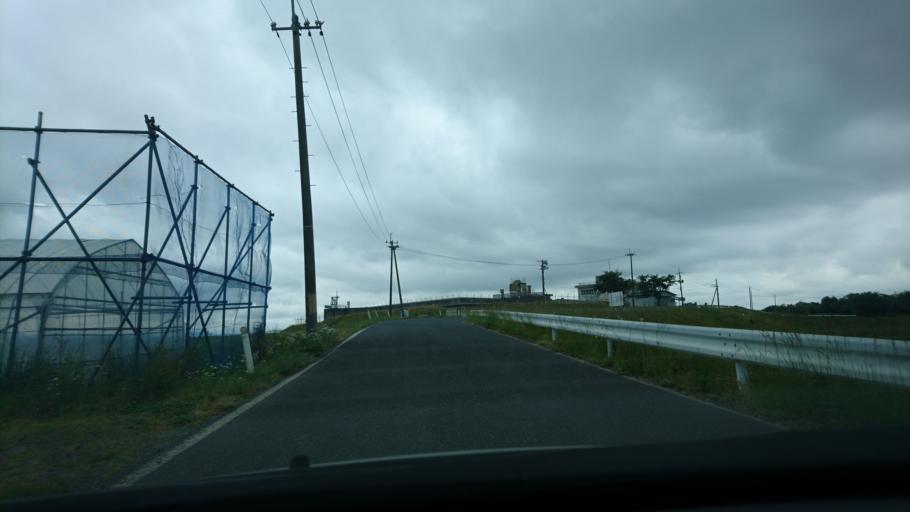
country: JP
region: Iwate
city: Ichinoseki
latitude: 38.8807
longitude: 141.2005
